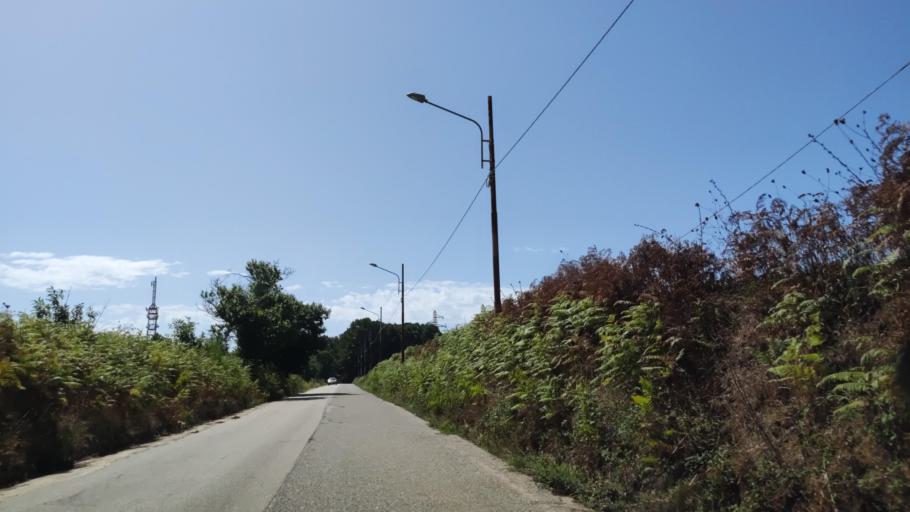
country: IT
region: Calabria
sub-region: Provincia di Reggio Calabria
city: Seminara
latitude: 38.3444
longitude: 15.8435
